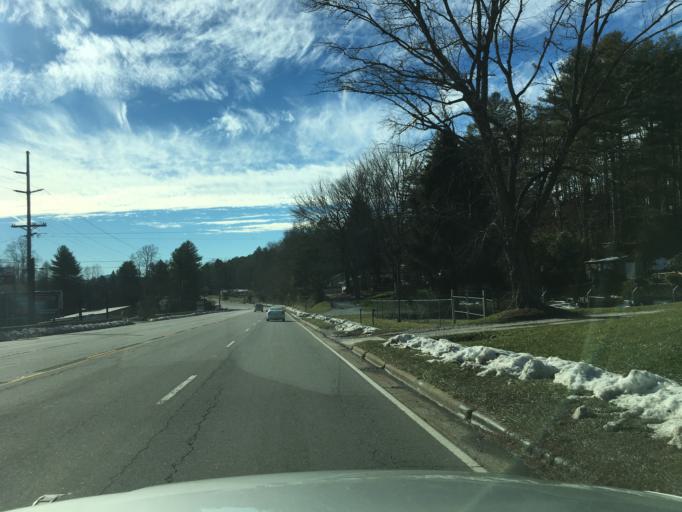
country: US
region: North Carolina
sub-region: Transylvania County
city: Brevard
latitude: 35.2140
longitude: -82.7584
